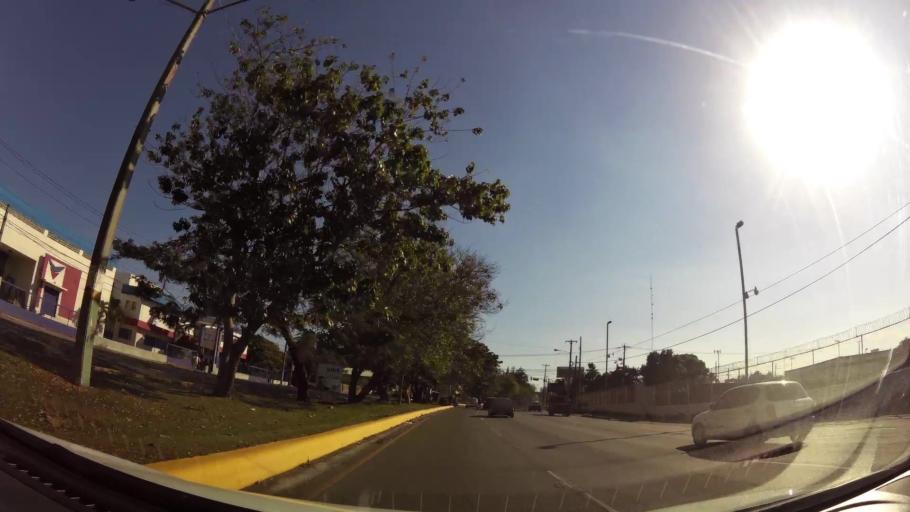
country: DO
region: Nacional
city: Bella Vista
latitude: 18.4546
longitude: -69.9719
